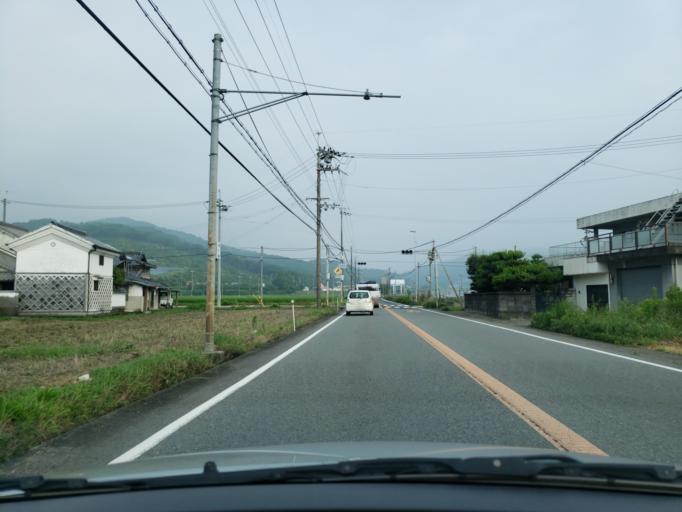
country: JP
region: Hyogo
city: Kariya
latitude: 34.8341
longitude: 134.3496
